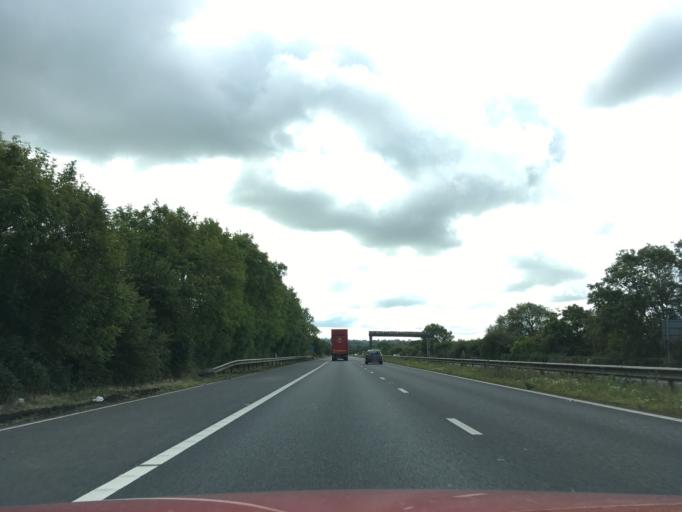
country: GB
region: England
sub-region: South Gloucestershire
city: Almondsbury
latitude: 51.5819
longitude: -2.5927
